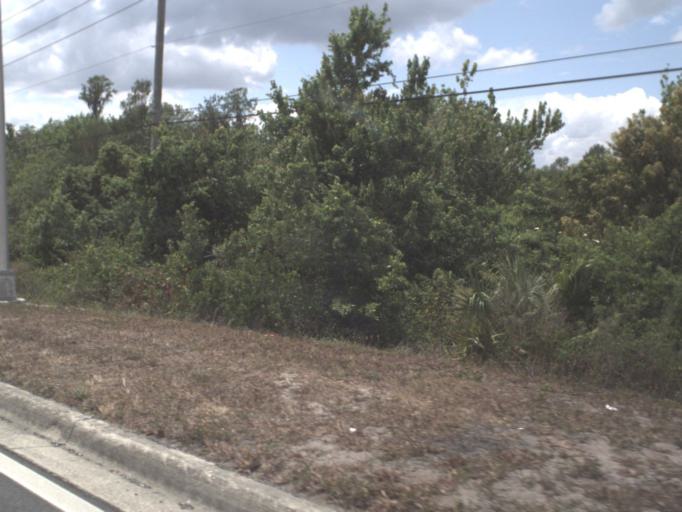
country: US
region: Florida
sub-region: Orange County
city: Meadow Woods
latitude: 28.3791
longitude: -81.3093
